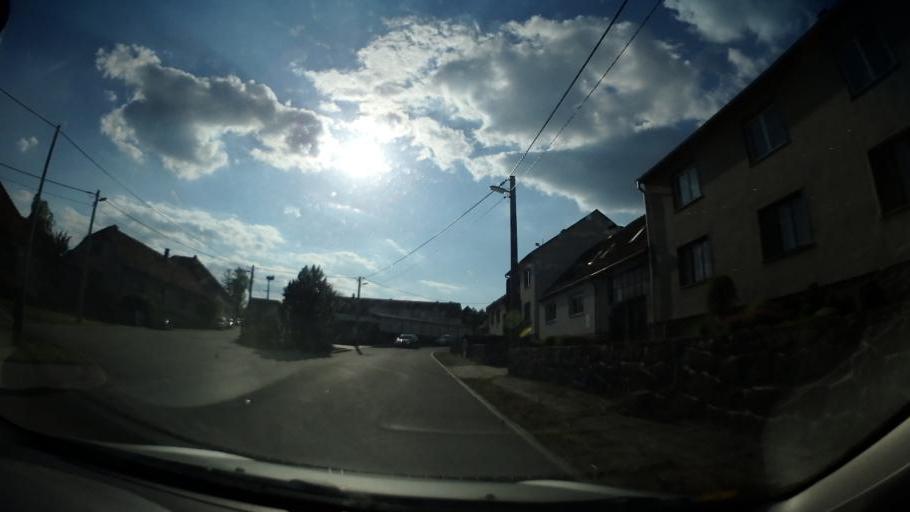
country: CZ
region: Vysocina
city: Budisov
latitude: 49.2943
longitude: 15.9827
